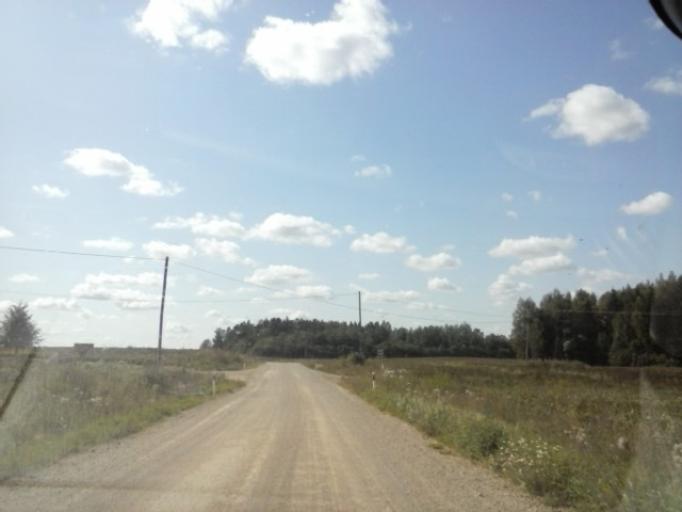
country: EE
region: Polvamaa
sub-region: Polva linn
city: Polva
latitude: 58.1067
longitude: 26.8598
